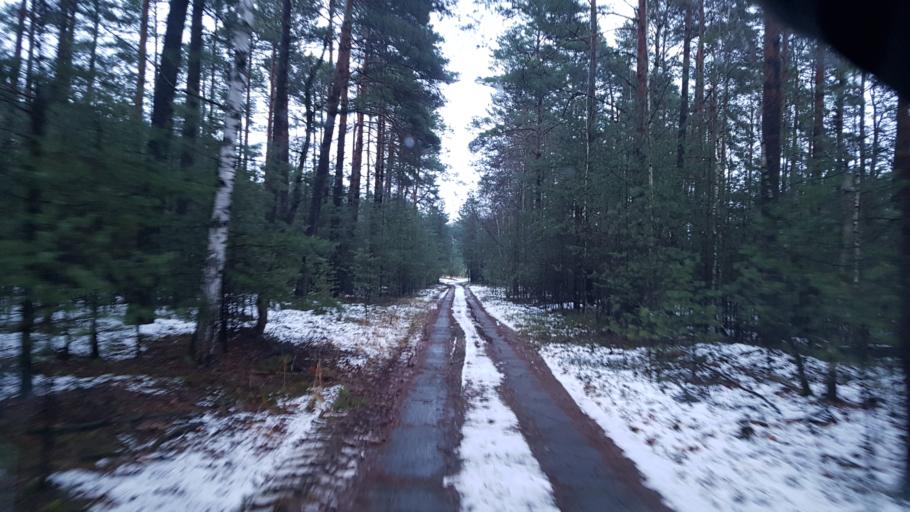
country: DE
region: Brandenburg
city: Janschwalde
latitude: 51.8838
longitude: 14.5612
